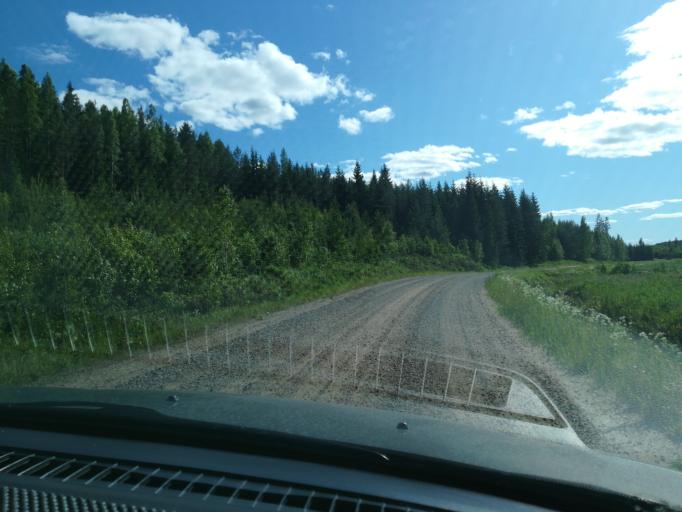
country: FI
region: Southern Savonia
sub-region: Mikkeli
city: Puumala
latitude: 61.6497
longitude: 28.1055
